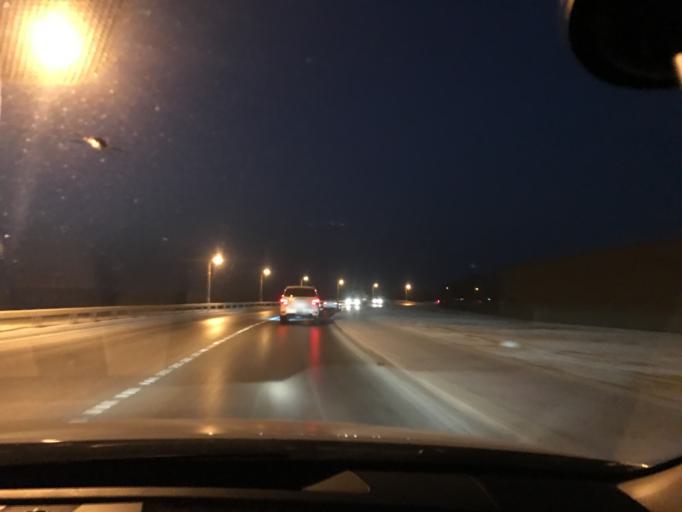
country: BH
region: Muharraq
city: Al Muharraq
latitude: 26.2810
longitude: 50.6131
